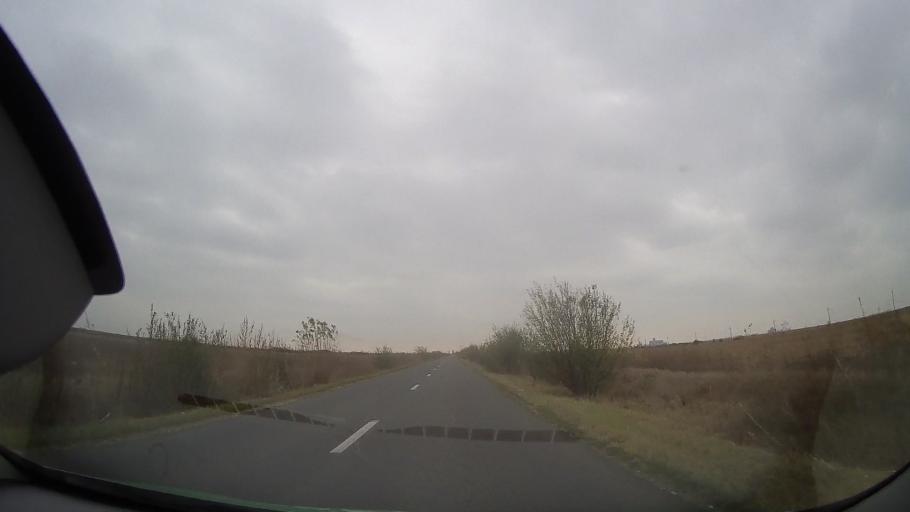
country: RO
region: Ialomita
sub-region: Comuna Manasia
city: Manasia
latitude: 44.7292
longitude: 26.6962
